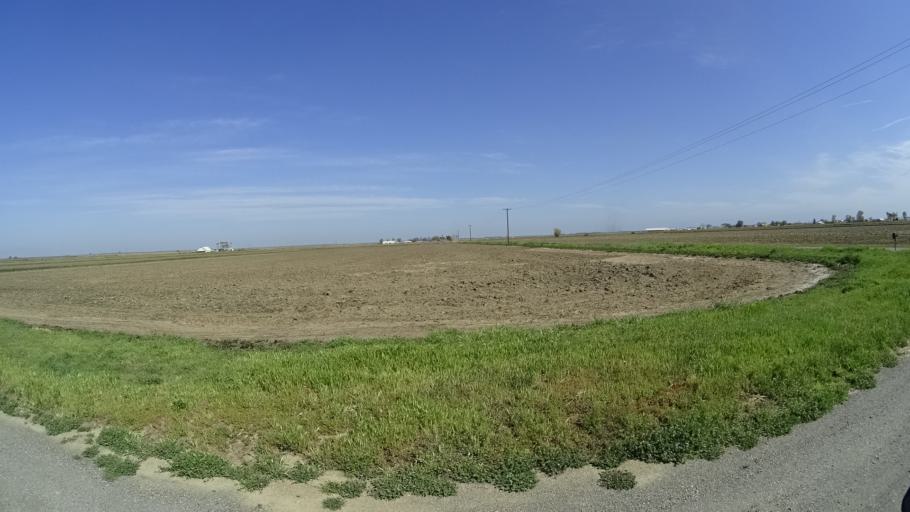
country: US
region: California
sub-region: Glenn County
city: Willows
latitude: 39.6090
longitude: -122.0748
